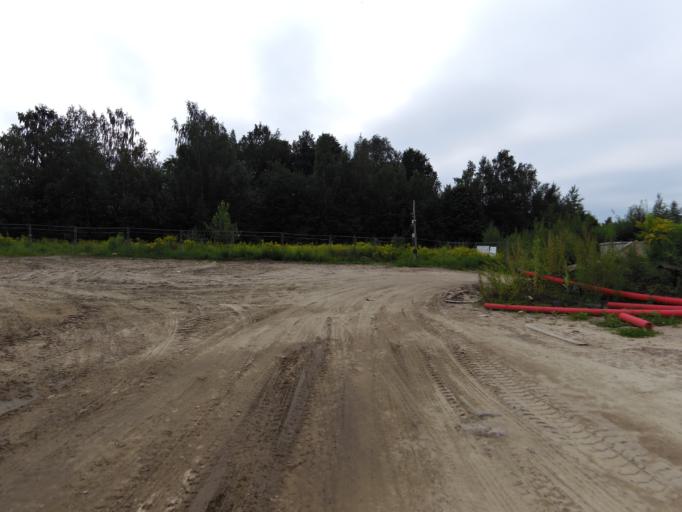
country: LT
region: Vilnius County
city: Rasos
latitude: 54.6578
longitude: 25.2942
